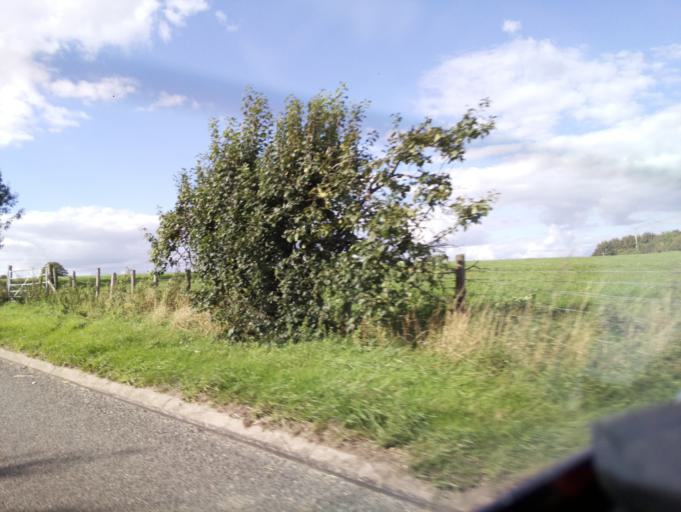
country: GB
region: England
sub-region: Hampshire
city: Compton
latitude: 51.0425
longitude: -1.3361
